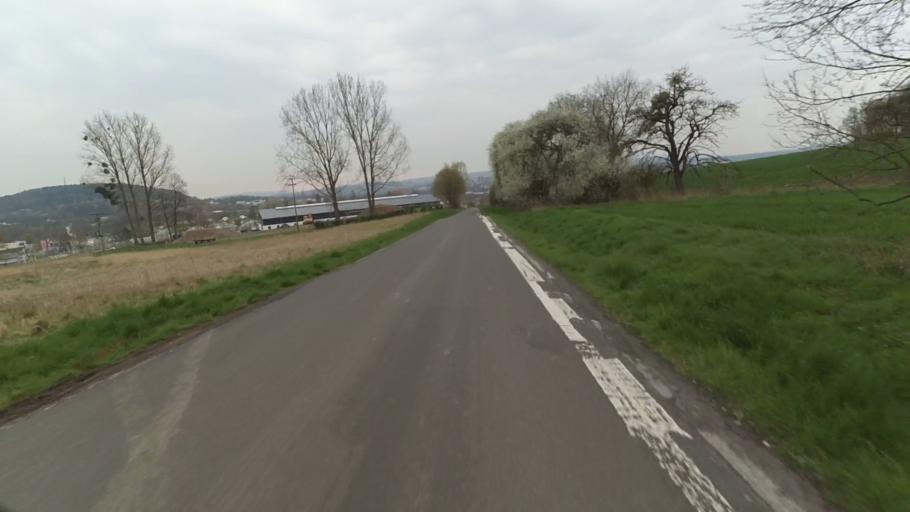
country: DE
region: Rheinland-Pfalz
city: Bannberscheid
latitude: 50.4510
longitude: 7.8299
